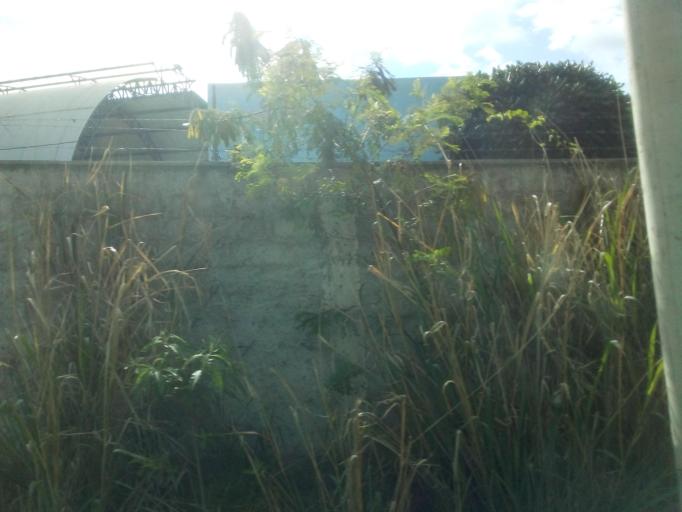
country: BR
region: Minas Gerais
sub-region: Belo Horizonte
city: Belo Horizonte
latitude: -19.8819
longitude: -43.8594
